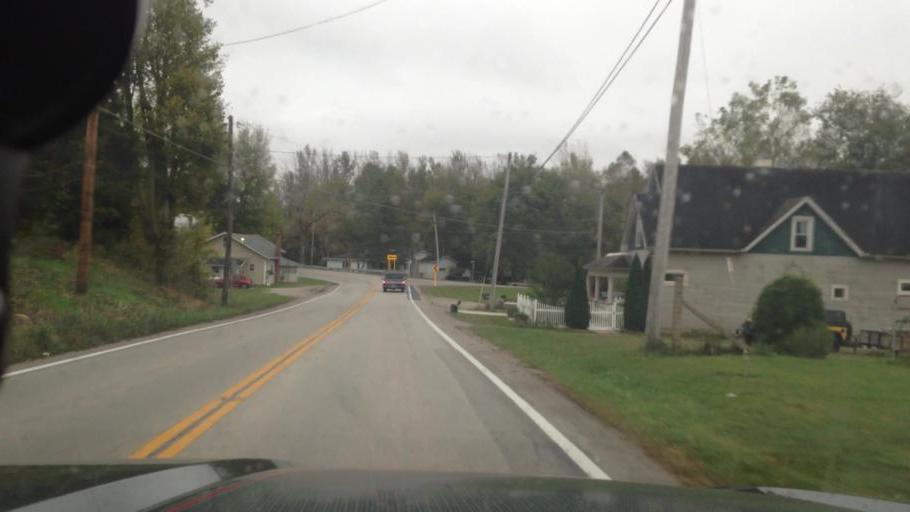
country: US
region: Ohio
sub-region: Darke County
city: Greenville
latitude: 40.1363
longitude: -84.7042
